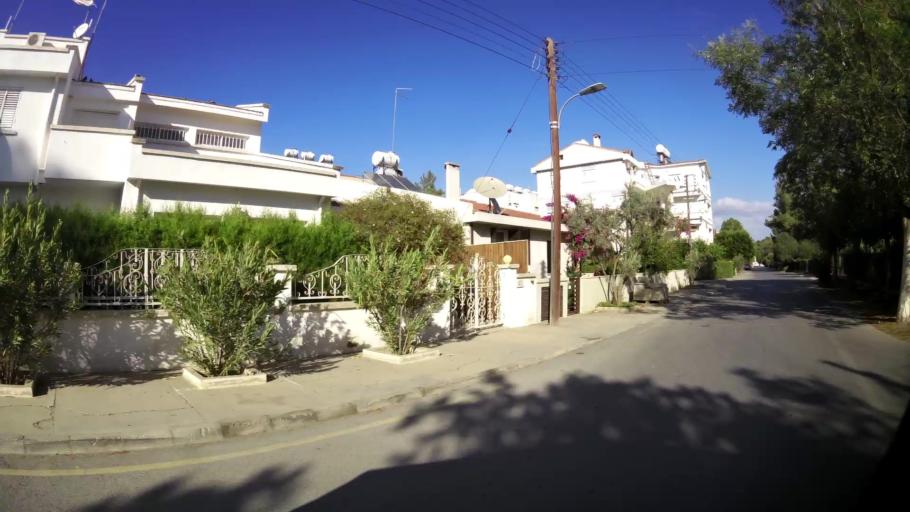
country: CY
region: Lefkosia
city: Nicosia
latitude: 35.1966
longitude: 33.3386
